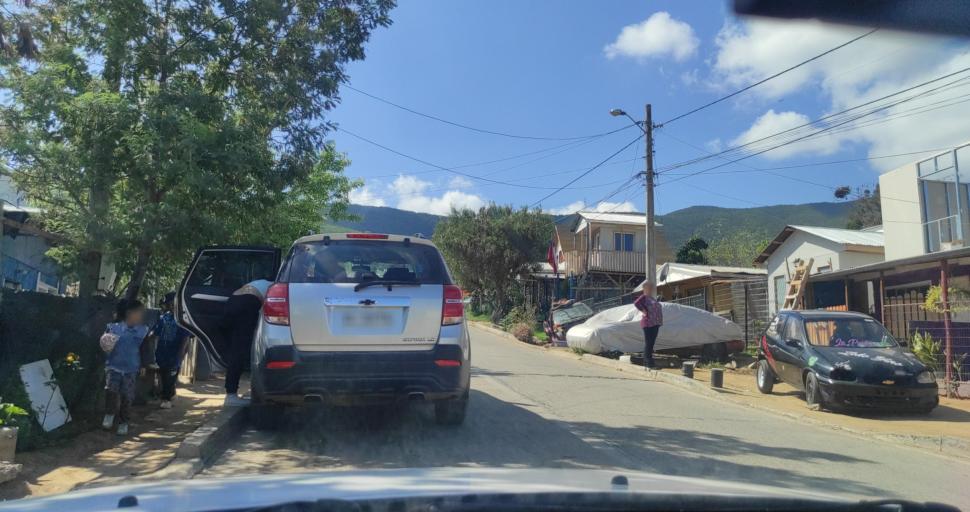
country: CL
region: Valparaiso
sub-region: Provincia de Marga Marga
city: Limache
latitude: -32.9869
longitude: -71.2247
